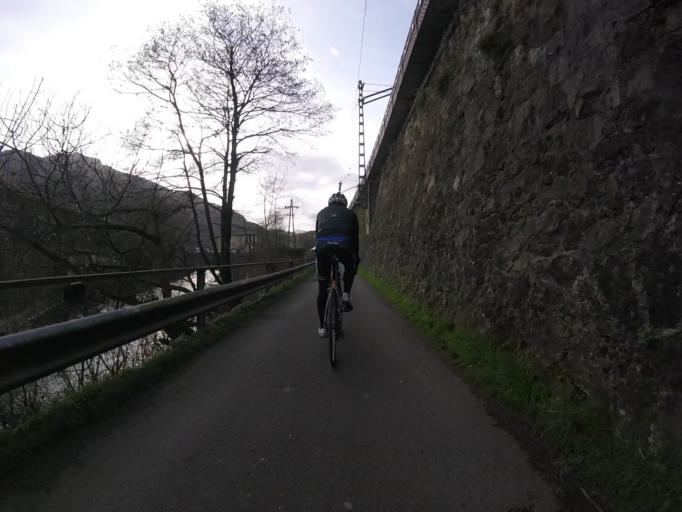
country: ES
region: Basque Country
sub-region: Provincia de Guipuzcoa
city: Anoeta
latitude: 43.1660
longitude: -2.0718
